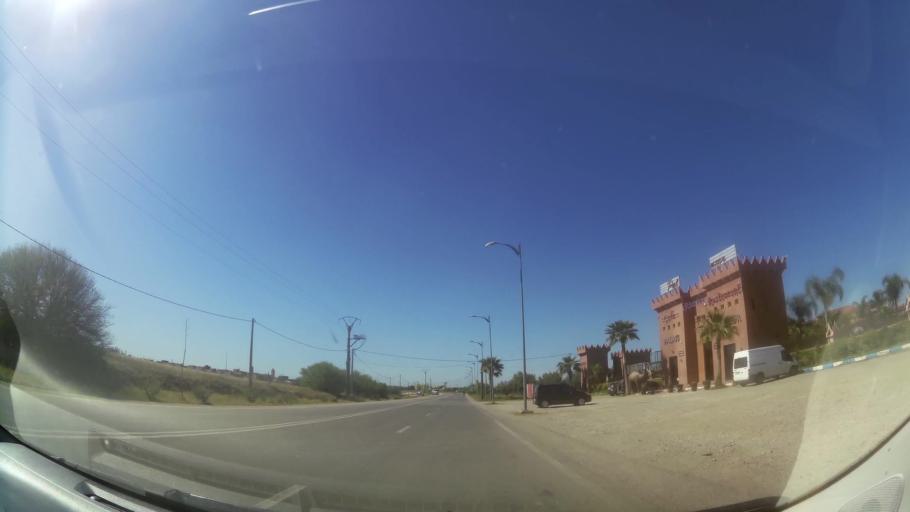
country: MA
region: Oriental
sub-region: Oujda-Angad
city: Oujda
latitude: 34.7171
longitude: -1.8642
